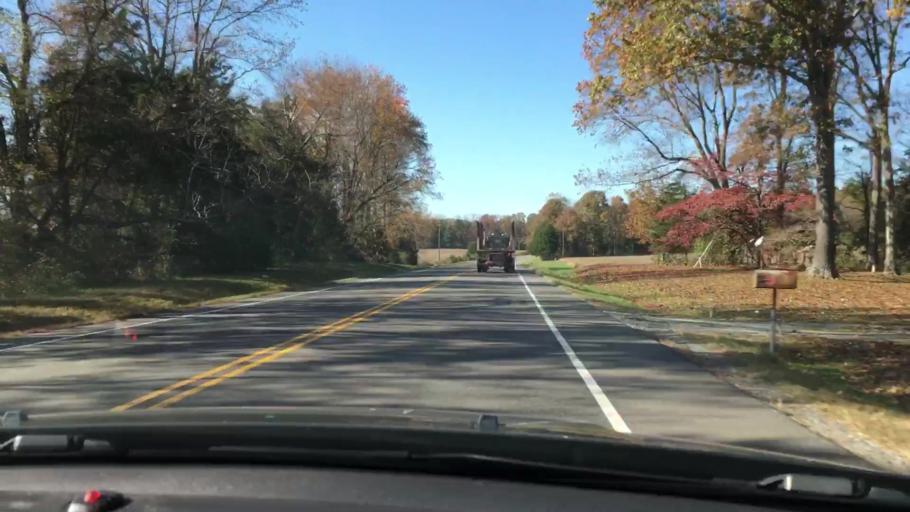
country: US
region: Virginia
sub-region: King William County
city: Central Garage
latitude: 37.7759
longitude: -77.1608
